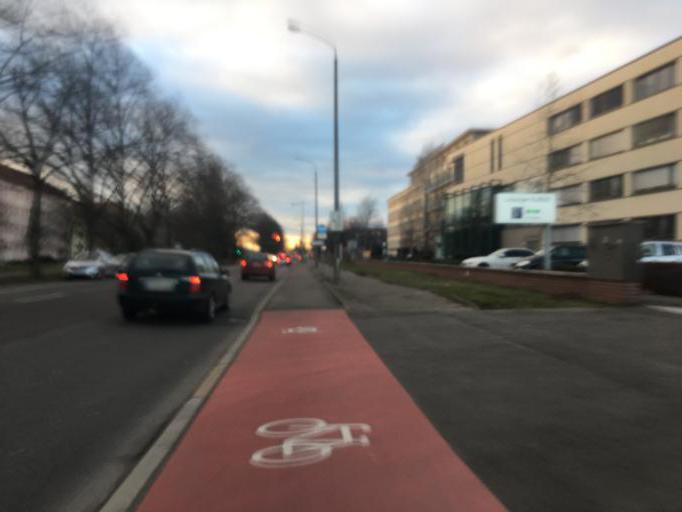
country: DE
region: Saxony
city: Taucha
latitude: 51.3513
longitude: 12.4329
